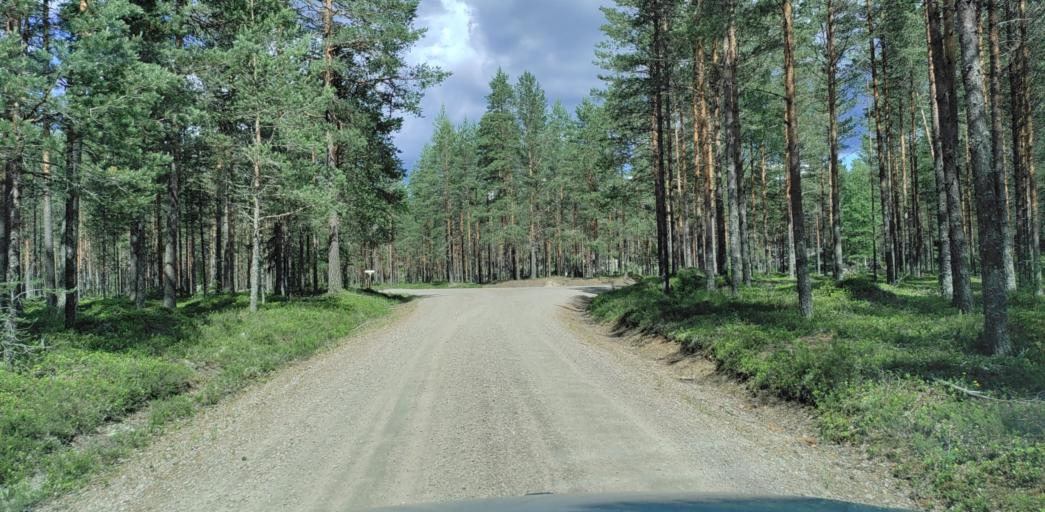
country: SE
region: Vaermland
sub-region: Hagfors Kommun
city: Ekshaerad
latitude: 60.0603
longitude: 13.2889
